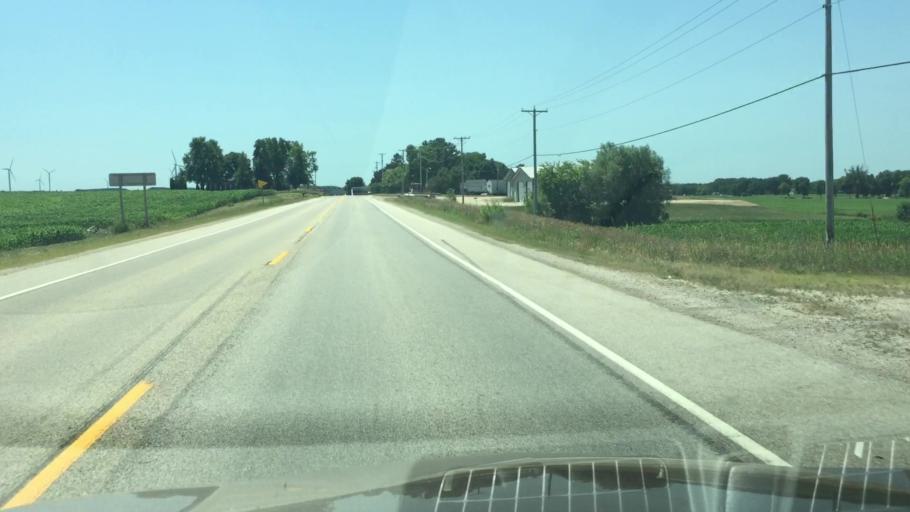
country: US
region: Wisconsin
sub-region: Fond du Lac County
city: Saint Peter
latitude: 43.9308
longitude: -88.3049
